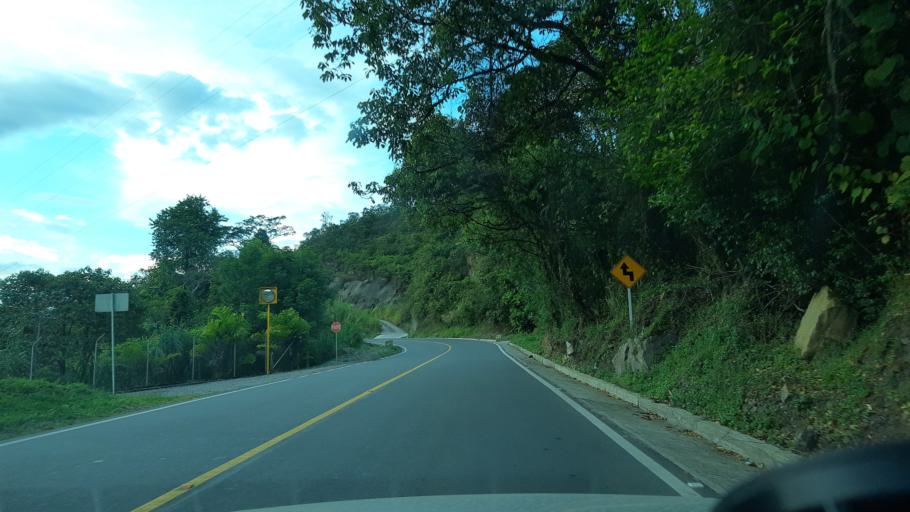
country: CO
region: Boyaca
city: Somondoco
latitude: 4.9935
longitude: -73.3509
